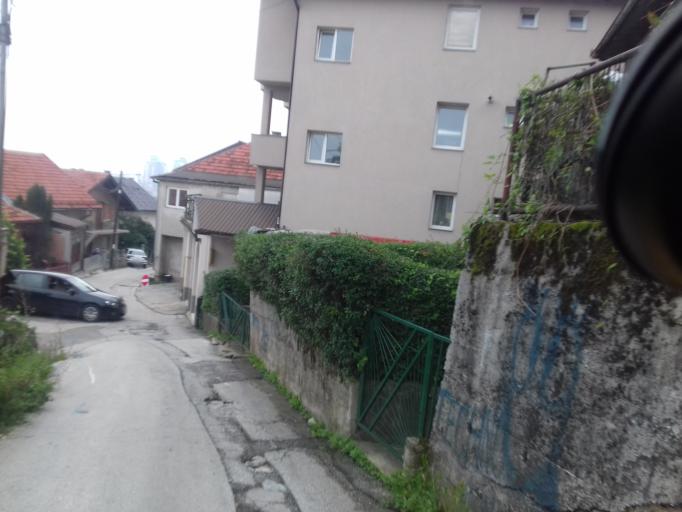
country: BA
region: Federation of Bosnia and Herzegovina
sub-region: Kanton Sarajevo
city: Sarajevo
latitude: 43.8404
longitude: 18.3572
